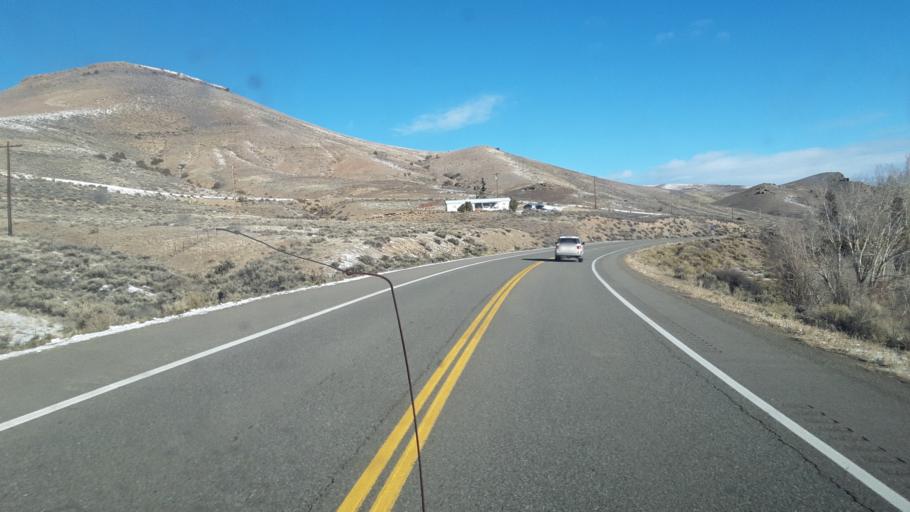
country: US
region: Colorado
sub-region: Gunnison County
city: Gunnison
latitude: 38.5054
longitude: -107.0272
